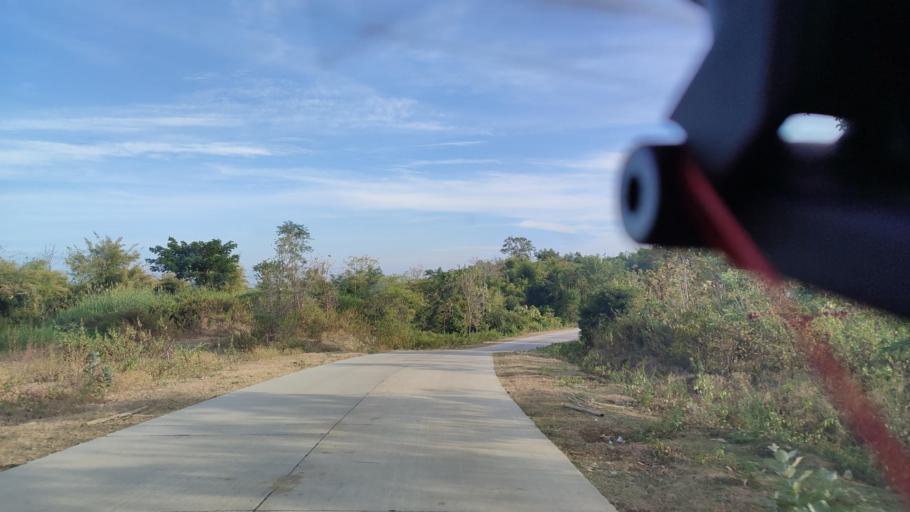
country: MM
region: Magway
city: Taungdwingyi
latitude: 20.0446
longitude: 95.7791
